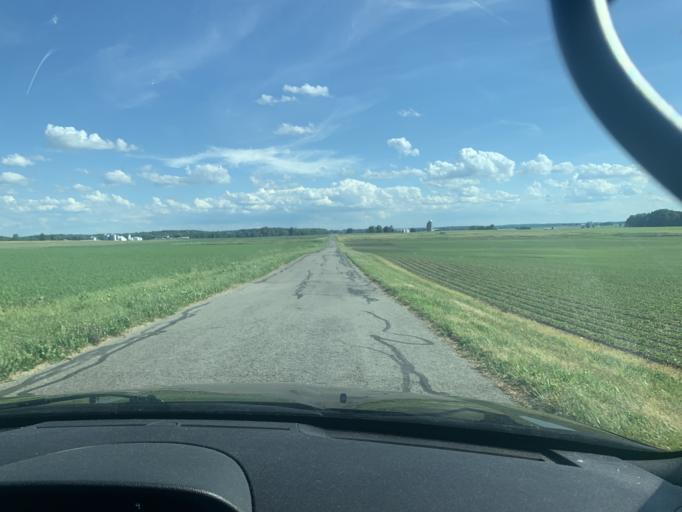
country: US
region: Ohio
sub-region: Logan County
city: De Graff
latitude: 40.3349
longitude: -83.8722
